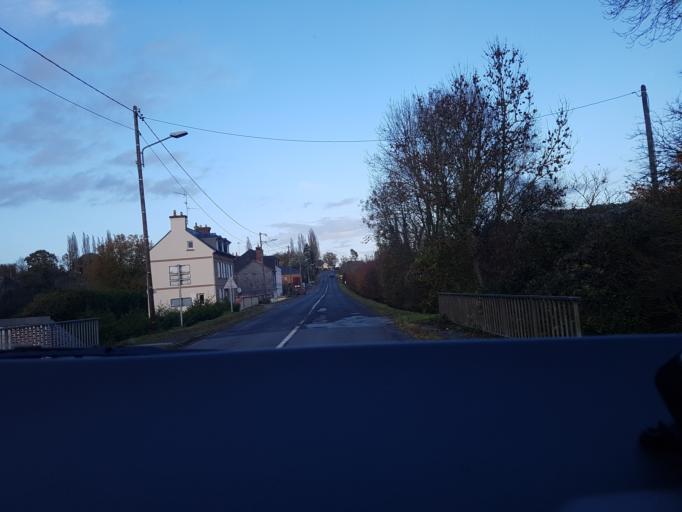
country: FR
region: Lower Normandy
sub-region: Departement du Calvados
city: Dozule
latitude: 49.2343
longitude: -0.0371
